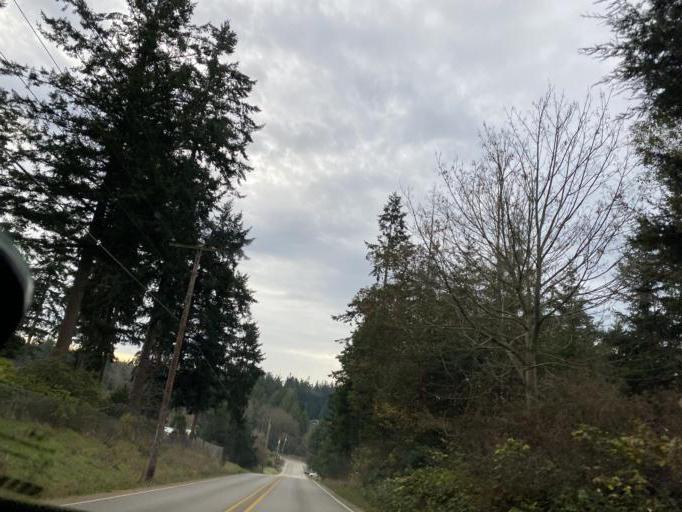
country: US
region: Washington
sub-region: Island County
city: Freeland
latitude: 47.9962
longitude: -122.5370
